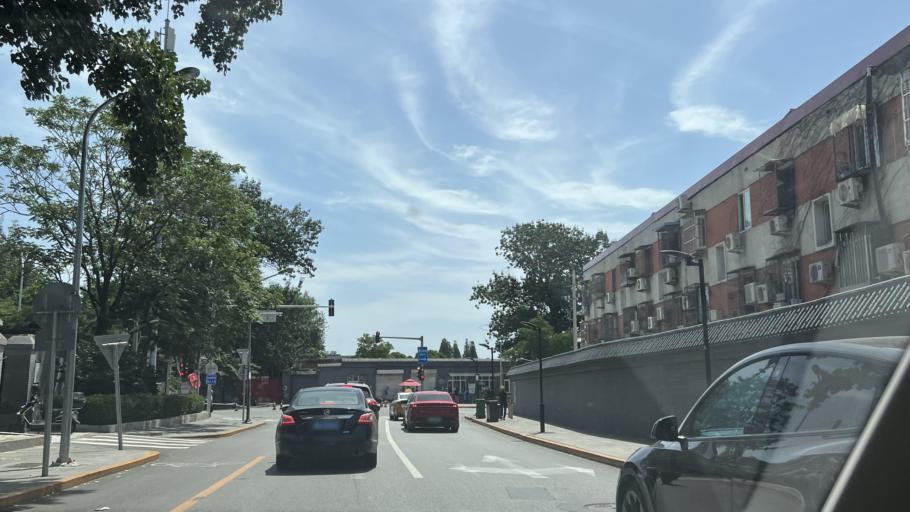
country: CN
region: Beijing
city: Xiangshan
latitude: 39.9914
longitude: 116.2032
